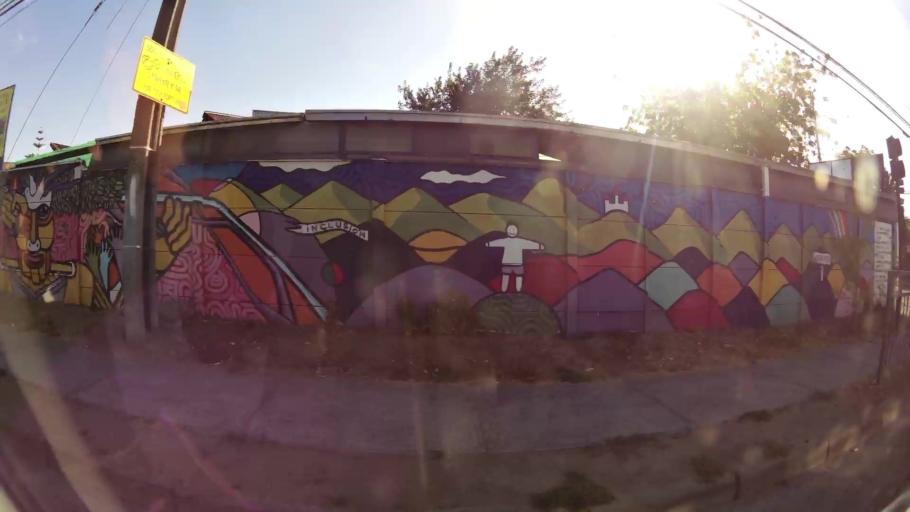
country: CL
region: Maule
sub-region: Provincia de Talca
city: Talca
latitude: -35.4306
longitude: -71.6711
